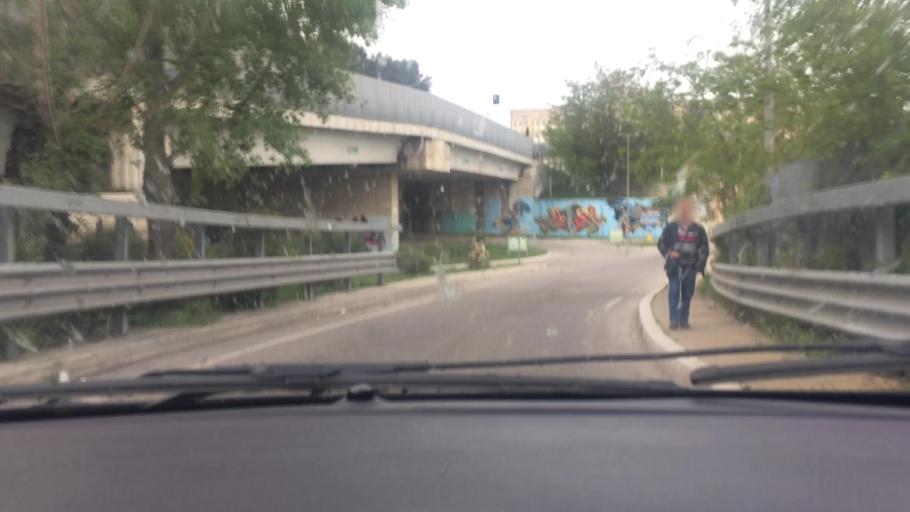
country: IT
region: Basilicate
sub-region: Provincia di Potenza
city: Potenza
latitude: 40.6521
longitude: 15.8016
